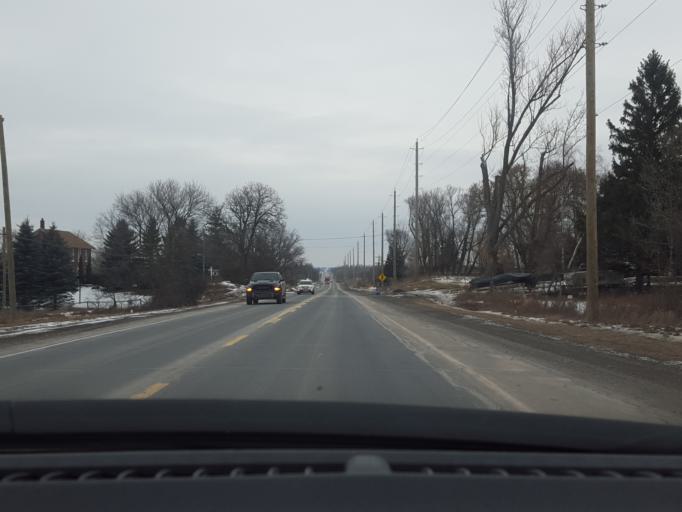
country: CA
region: Ontario
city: Keswick
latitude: 44.1766
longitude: -79.4341
